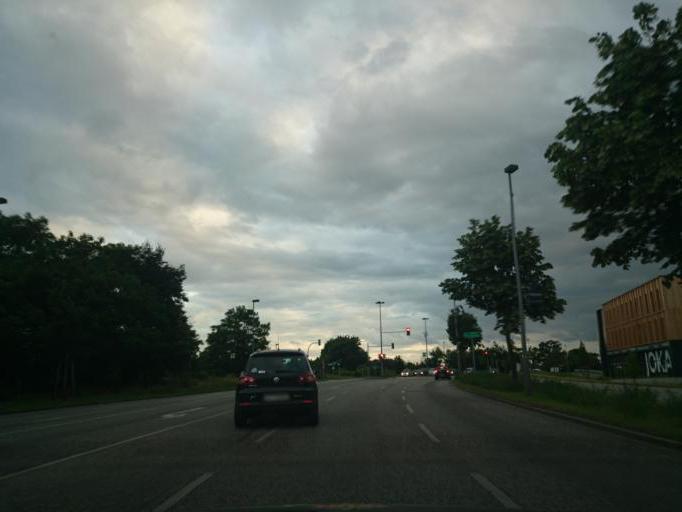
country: DE
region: Berlin
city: Adlershof
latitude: 52.4263
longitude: 13.5462
